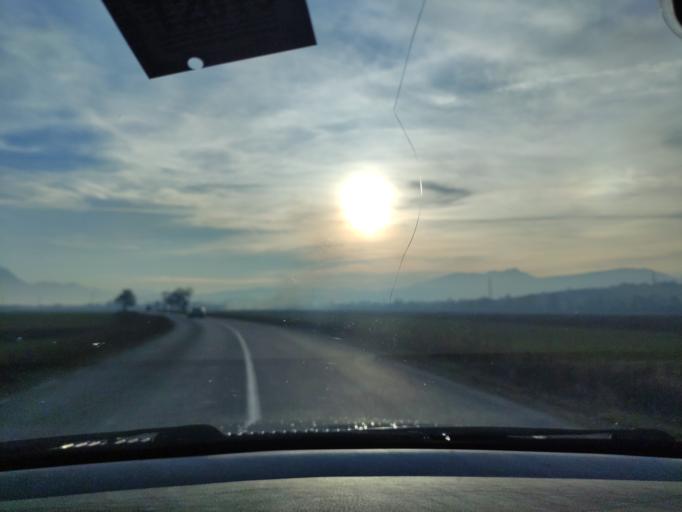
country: RO
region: Brasov
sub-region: Comuna Vulcan
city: Vulcan
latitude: 45.6489
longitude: 25.4295
